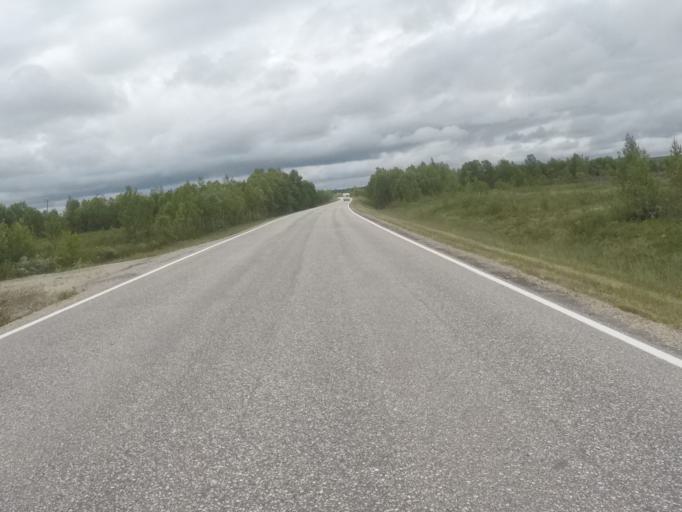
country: FI
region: Lapland
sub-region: Tunturi-Lappi
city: Enontekioe
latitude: 68.4839
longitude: 23.3588
